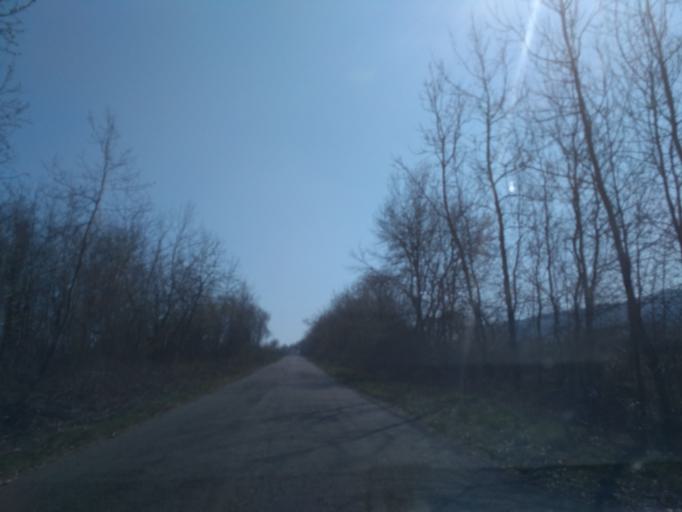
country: SK
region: Presovsky
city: Vranov nad Topl'ou
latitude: 48.8192
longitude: 21.6377
